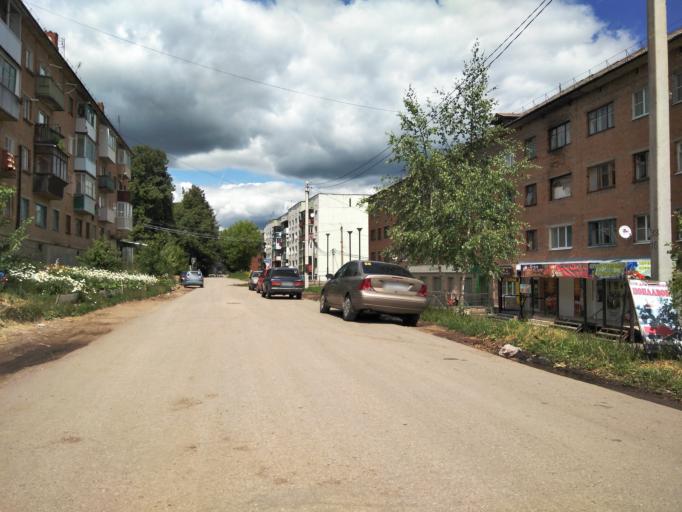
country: RU
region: Tula
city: Lomintsevskiy
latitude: 53.9348
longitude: 37.6342
